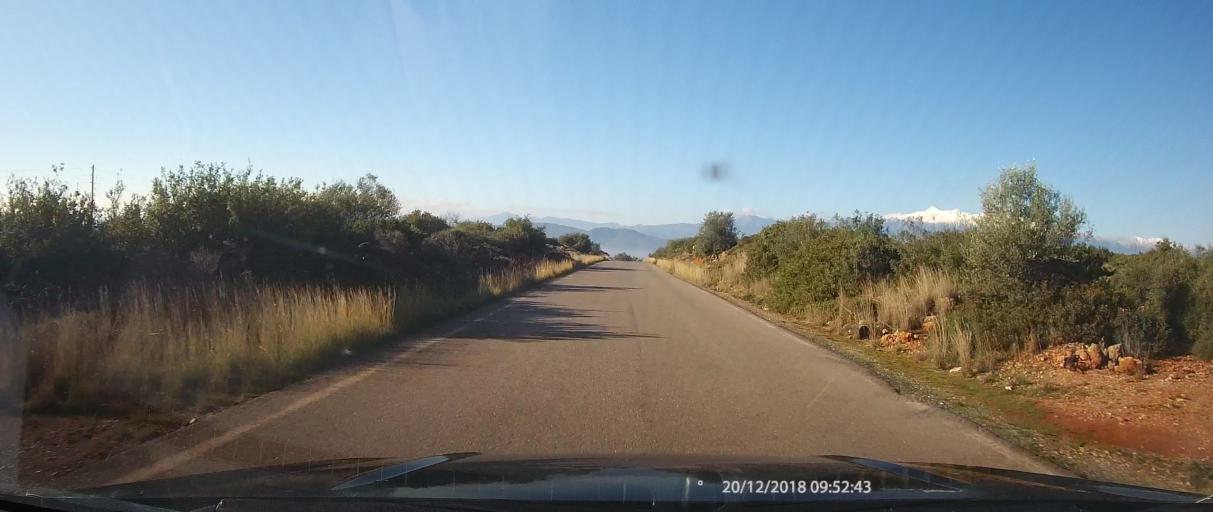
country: GR
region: Peloponnese
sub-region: Nomos Lakonias
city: Yerakion
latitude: 37.0089
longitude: 22.6405
